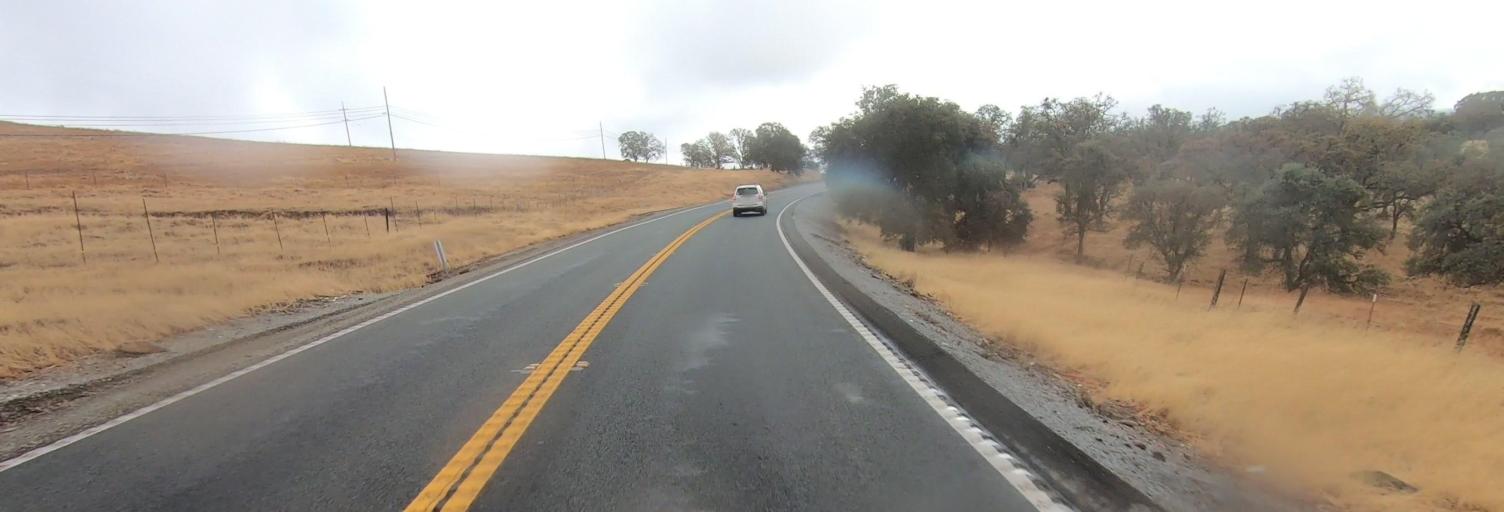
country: US
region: California
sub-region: Calaveras County
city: San Andreas
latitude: 38.2119
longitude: -120.7468
